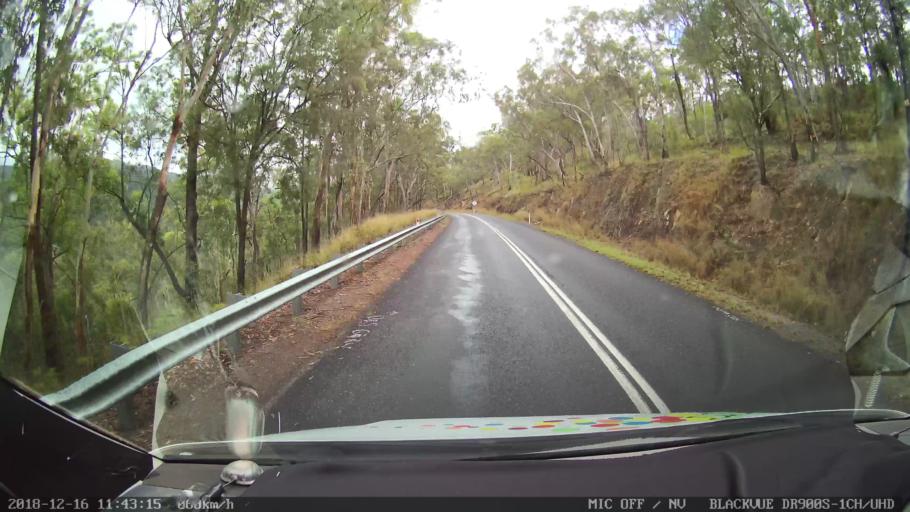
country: AU
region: New South Wales
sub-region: Tenterfield Municipality
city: Carrolls Creek
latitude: -28.9468
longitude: 152.2158
